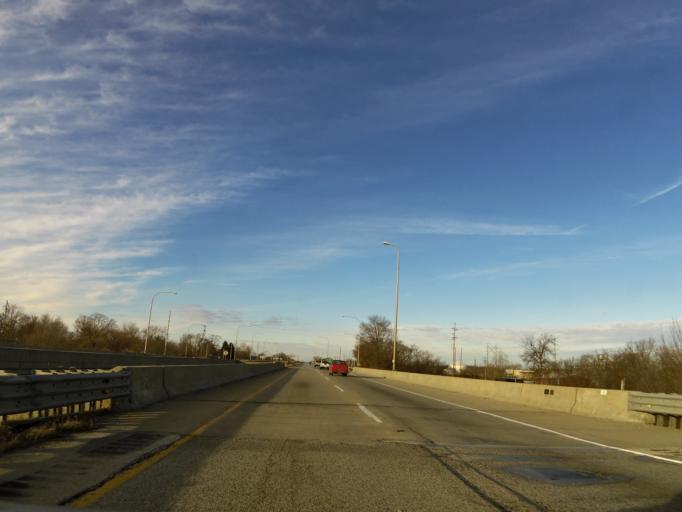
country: US
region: Illinois
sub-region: Vermilion County
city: Tilton
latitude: 40.1050
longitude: -87.6452
